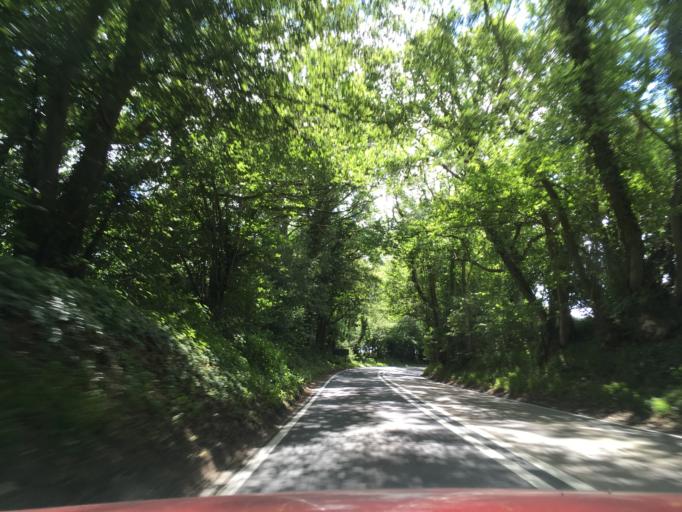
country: GB
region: England
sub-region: Hampshire
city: Highclere
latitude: 51.3196
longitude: -1.3833
